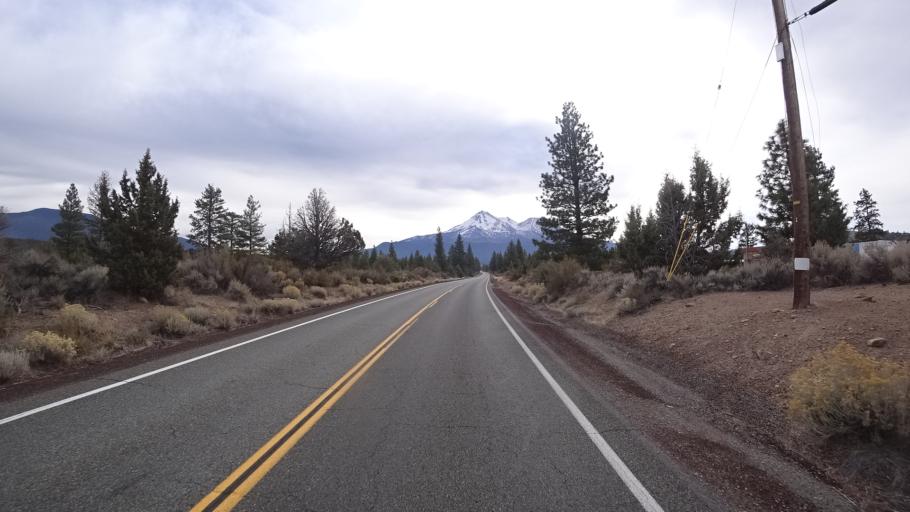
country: US
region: California
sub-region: Siskiyou County
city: Weed
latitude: 41.5501
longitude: -122.2490
